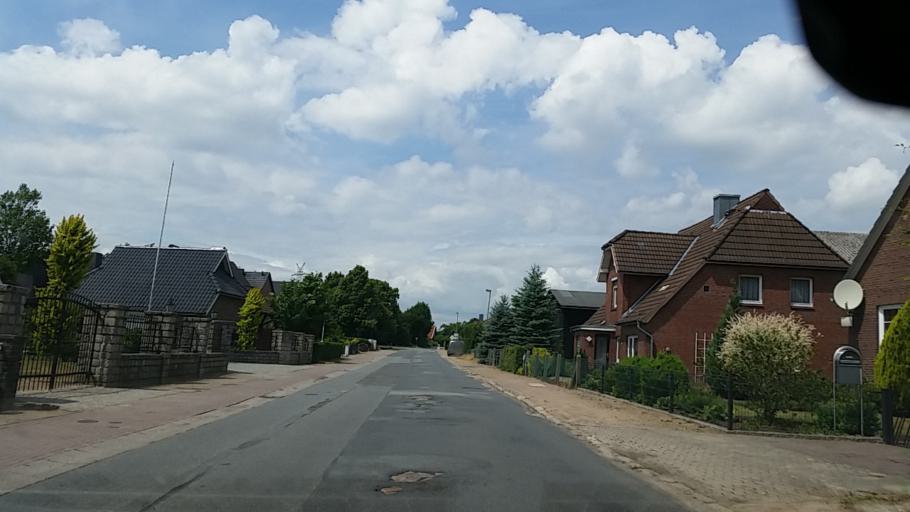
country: DE
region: Schleswig-Holstein
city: Tremsbuttel
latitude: 53.7371
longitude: 10.3011
